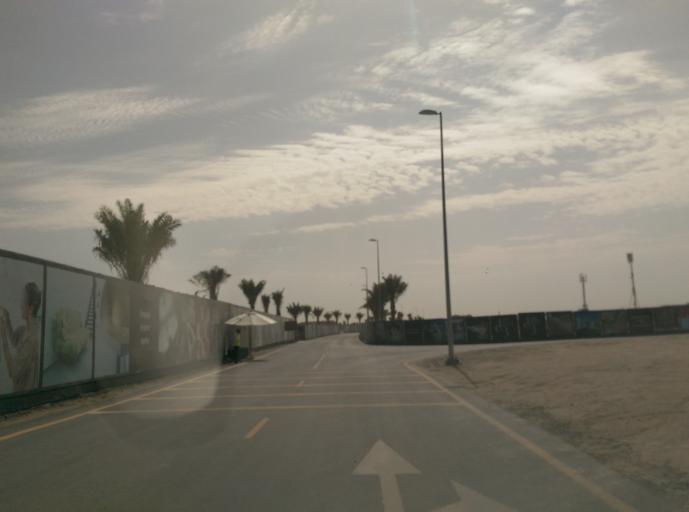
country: AE
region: Dubai
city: Dubai
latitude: 25.1894
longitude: 55.2999
